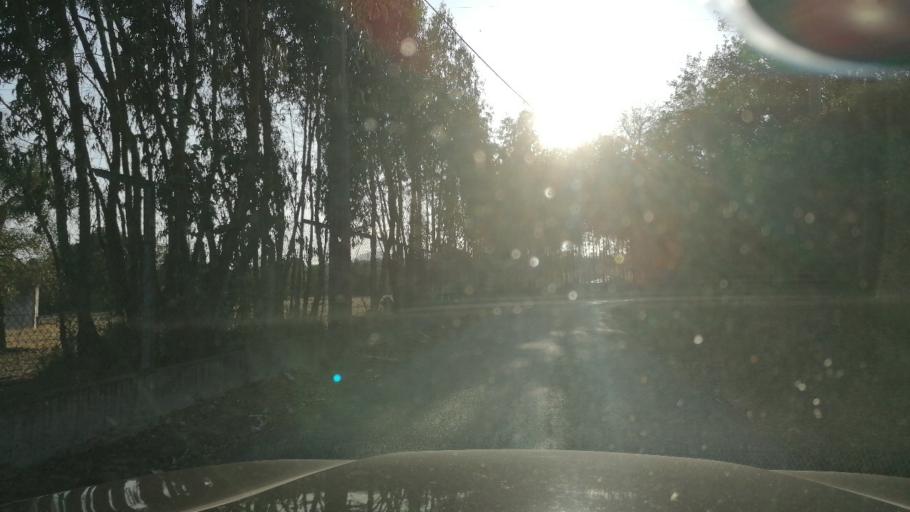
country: PT
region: Setubal
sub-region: Setubal
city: Setubal
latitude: 38.5488
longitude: -8.8463
